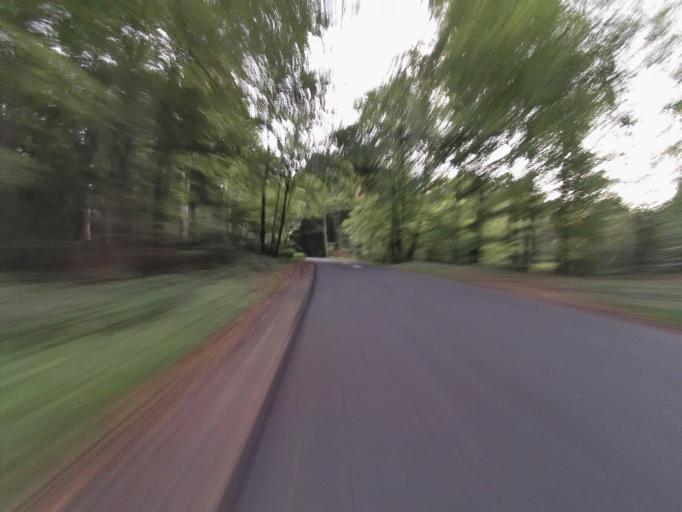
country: DE
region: North Rhine-Westphalia
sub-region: Regierungsbezirk Munster
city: Tecklenburg
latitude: 52.2346
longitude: 7.8129
